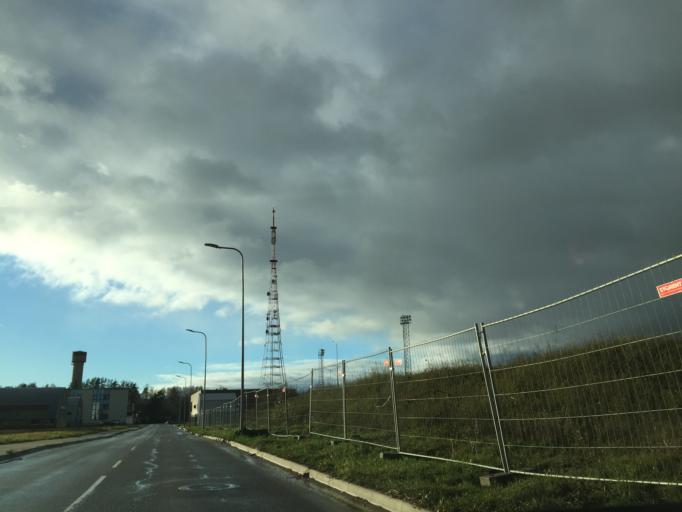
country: LV
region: Valmieras Rajons
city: Valmiera
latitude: 57.5291
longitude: 25.3935
